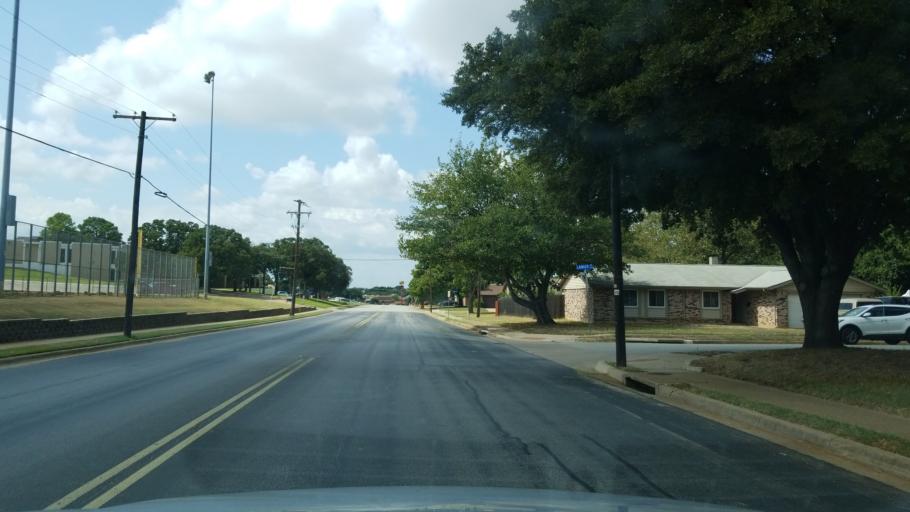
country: US
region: Texas
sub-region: Tarrant County
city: Euless
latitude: 32.8453
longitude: -97.0957
